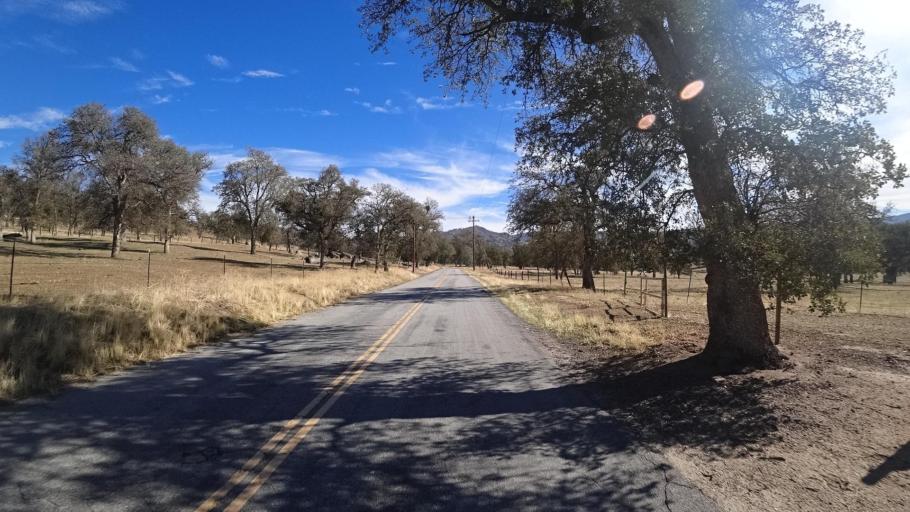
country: US
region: California
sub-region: Kern County
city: Alta Sierra
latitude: 35.6223
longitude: -118.7430
